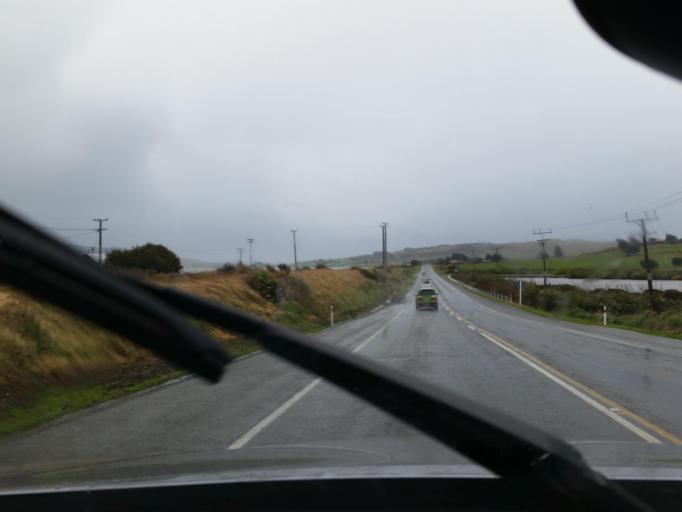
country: NZ
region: Southland
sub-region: Invercargill City
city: Bluff
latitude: -46.5468
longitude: 168.3009
